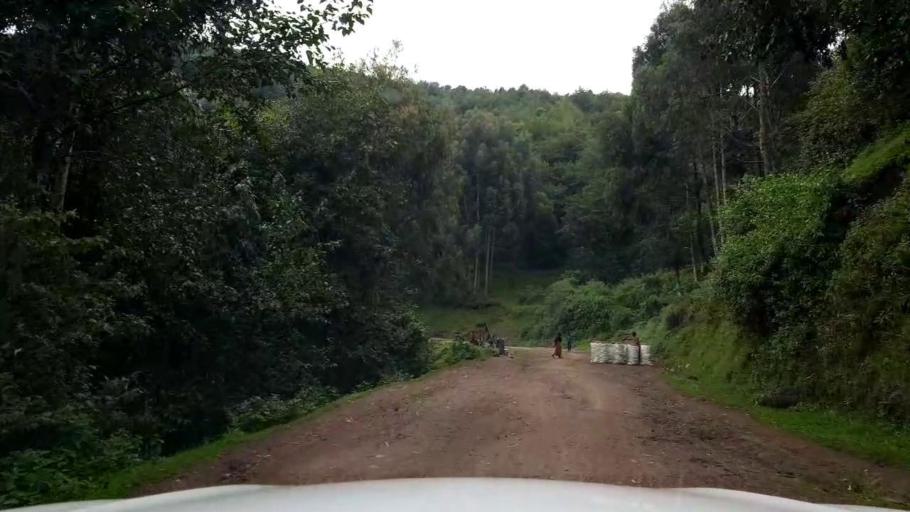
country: RW
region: Western Province
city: Gisenyi
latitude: -1.6592
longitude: 29.4188
